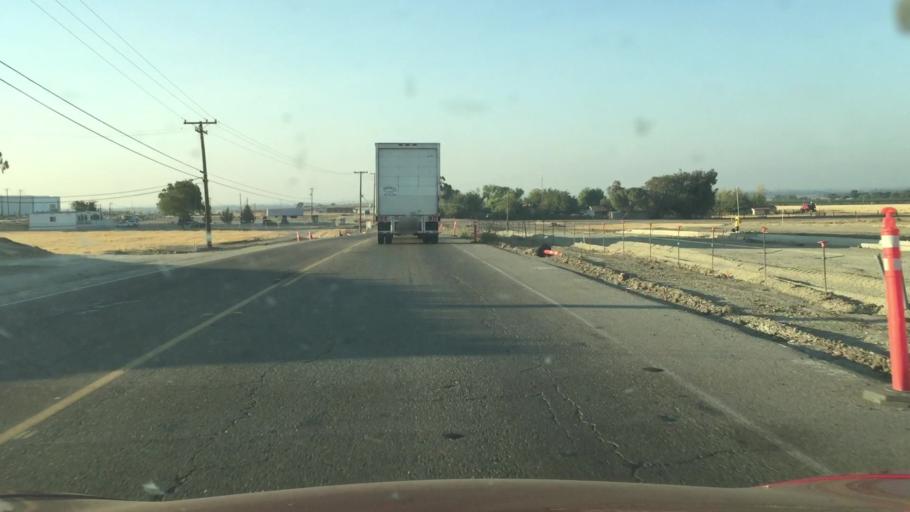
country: US
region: California
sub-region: San Joaquin County
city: Mountain House
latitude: 37.7339
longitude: -121.5315
